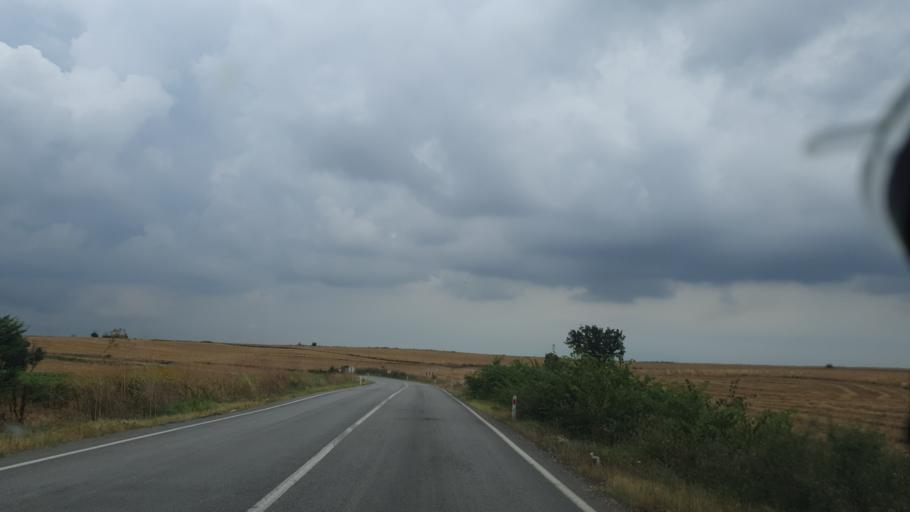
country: TR
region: Tekirdag
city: Hayrabolu
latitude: 41.2273
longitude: 27.0380
